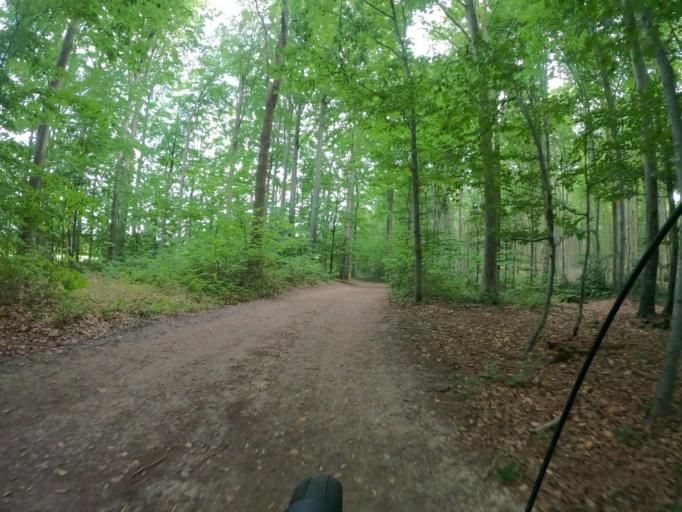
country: DE
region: Schleswig-Holstein
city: Steinberg
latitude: 54.7897
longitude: 9.7866
